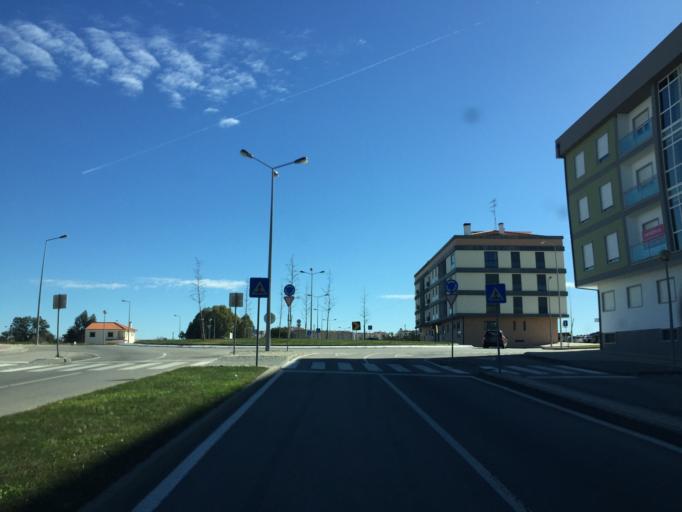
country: PT
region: Castelo Branco
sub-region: Castelo Branco
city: Castelo Branco
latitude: 39.8338
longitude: -7.4897
